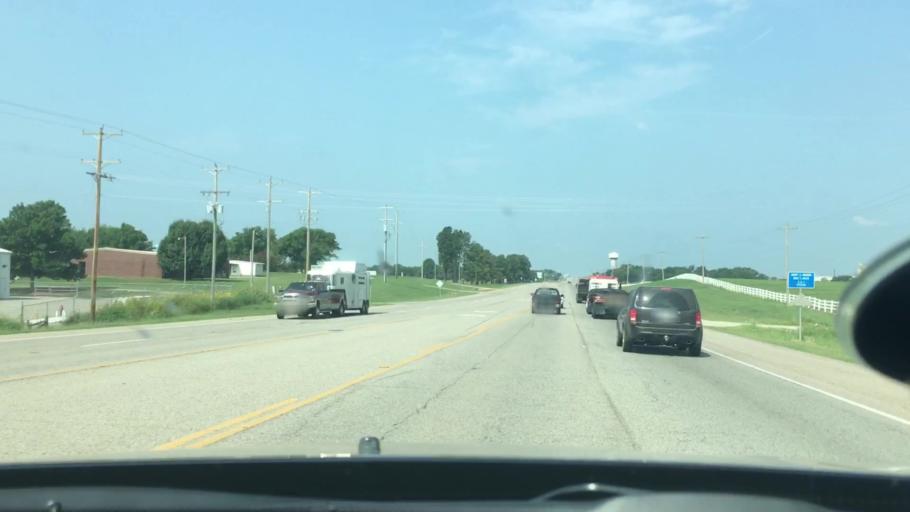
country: US
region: Oklahoma
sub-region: Bryan County
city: Durant
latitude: 33.9978
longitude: -96.4334
